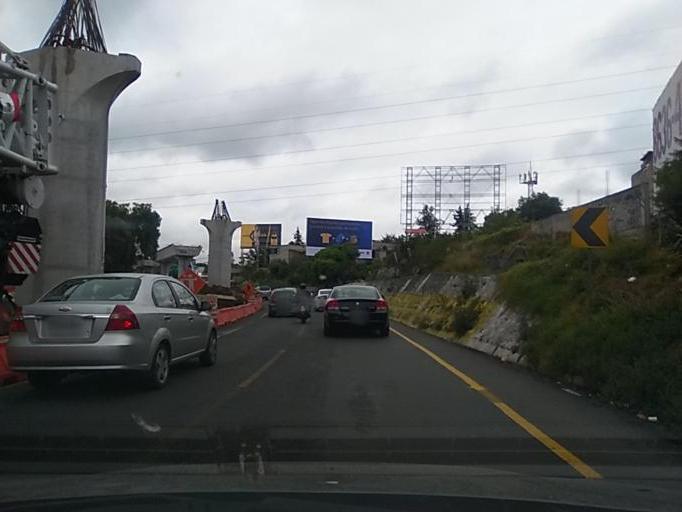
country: MX
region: Mexico City
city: Tlalpan
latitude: 19.2617
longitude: -99.1660
